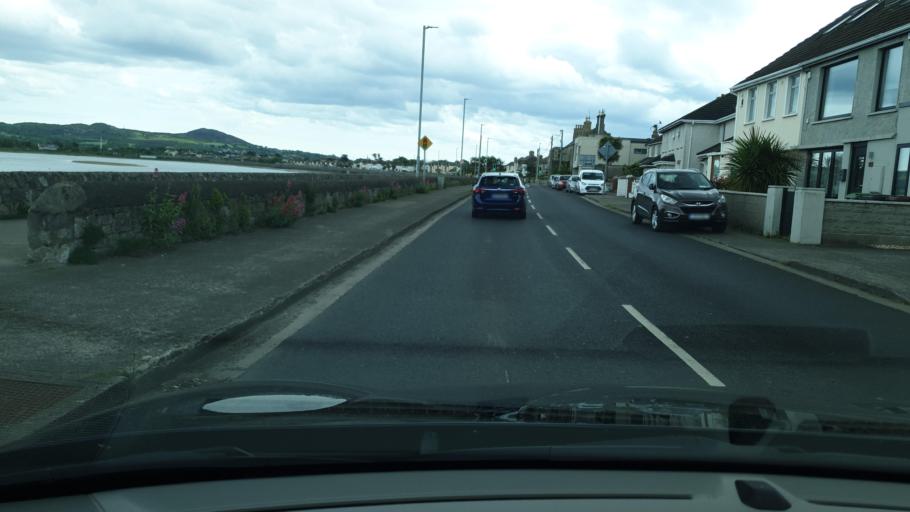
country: IE
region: Leinster
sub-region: Fingal County
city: Baldoyle
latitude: 53.3979
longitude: -6.1263
